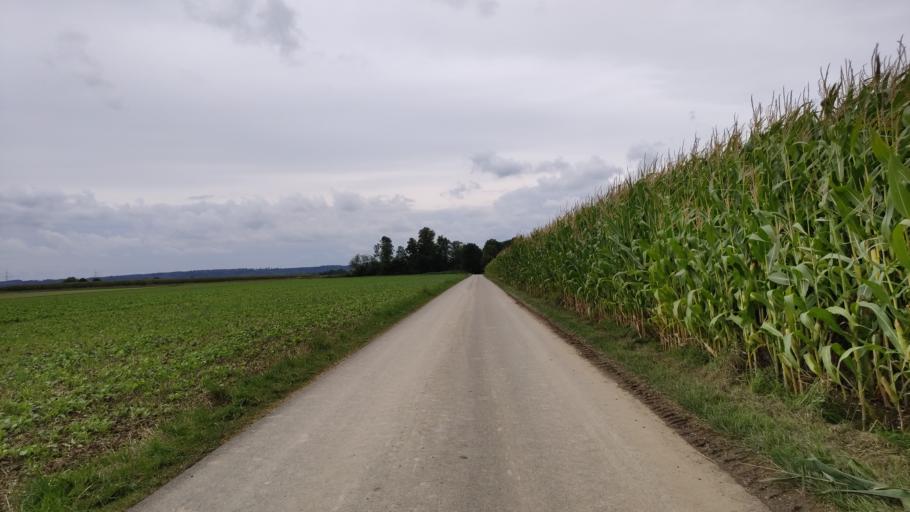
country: DE
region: Bavaria
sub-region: Swabia
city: Wehringen
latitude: 48.2368
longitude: 10.8191
